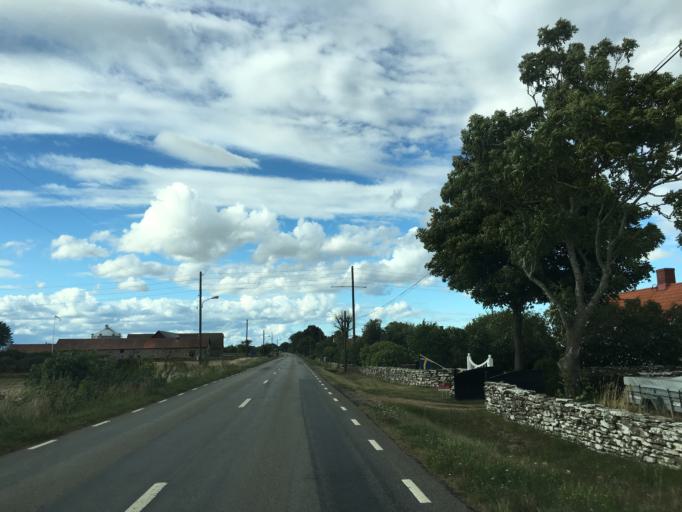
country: SE
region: Kalmar
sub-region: Morbylanga Kommun
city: Moerbylanga
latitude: 56.4187
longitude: 16.4351
